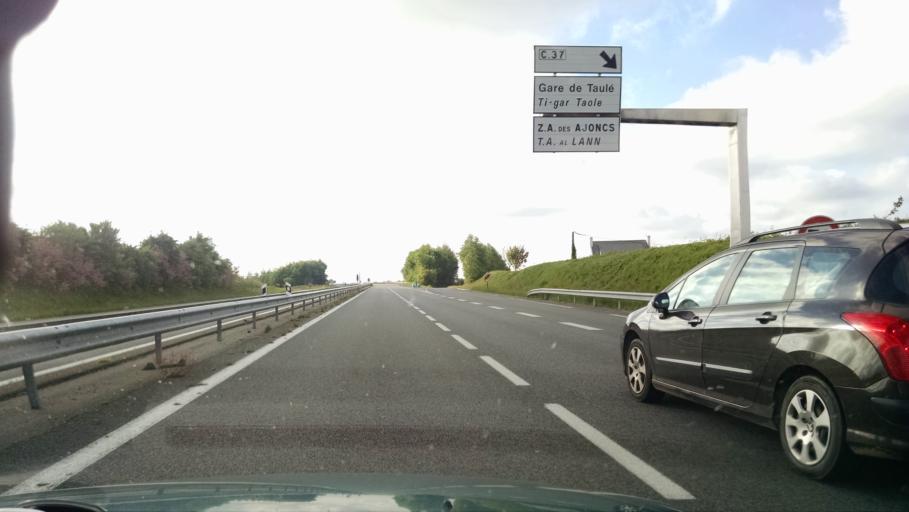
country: FR
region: Brittany
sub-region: Departement du Finistere
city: Taule
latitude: 48.6180
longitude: -3.8960
